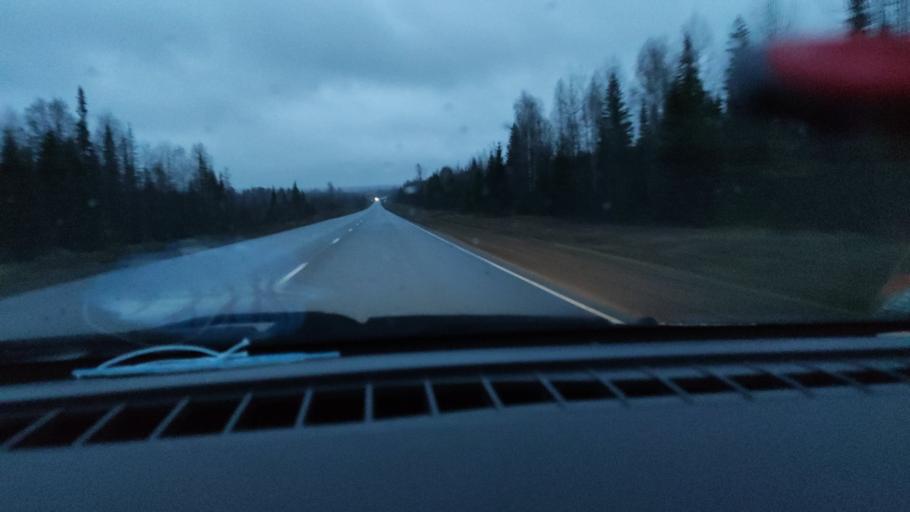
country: RU
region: Udmurtiya
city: Mozhga
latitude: 56.3295
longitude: 52.3090
